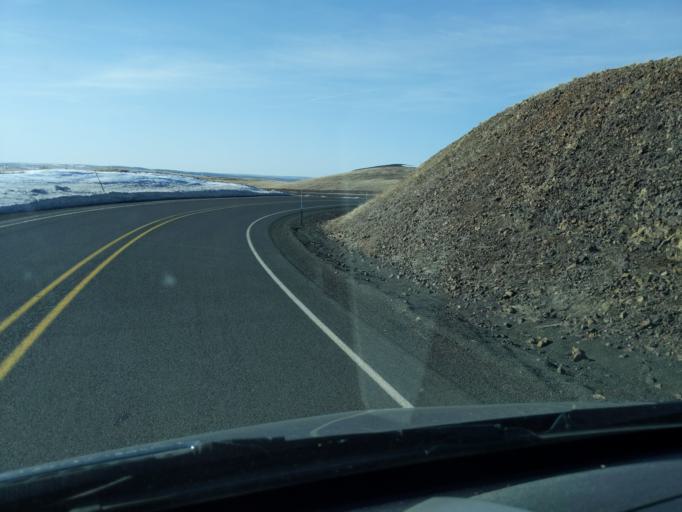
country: US
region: Oregon
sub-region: Umatilla County
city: Pilot Rock
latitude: 45.2977
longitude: -118.9847
